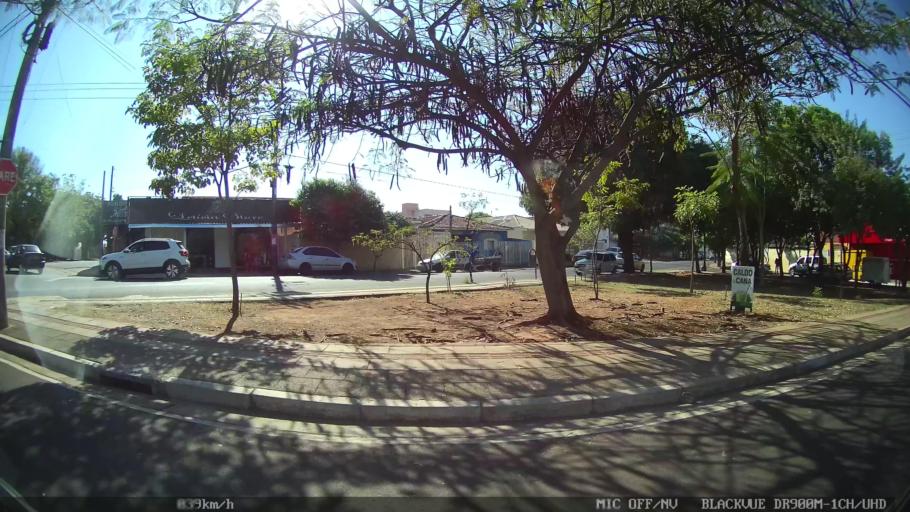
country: BR
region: Sao Paulo
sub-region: Sao Jose Do Rio Preto
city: Sao Jose do Rio Preto
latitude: -20.7860
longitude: -49.3912
